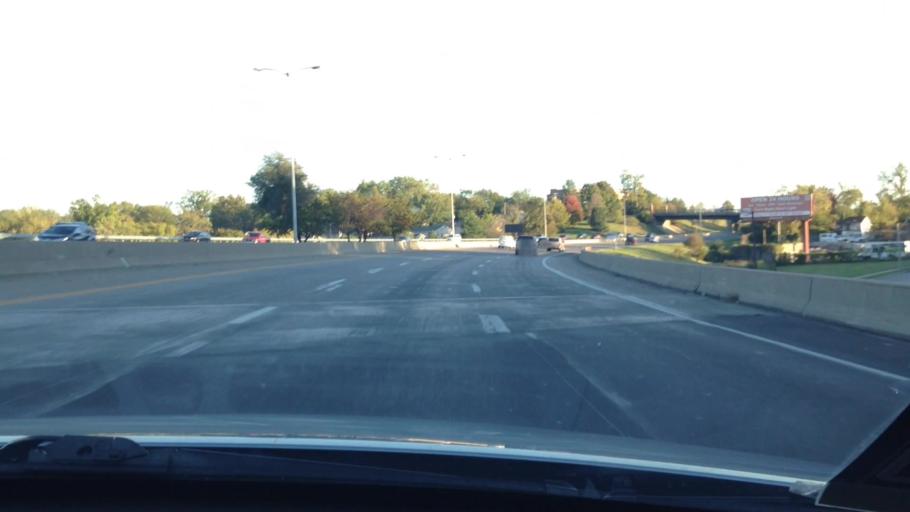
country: US
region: Kansas
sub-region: Johnson County
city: Westwood
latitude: 39.0370
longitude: -94.5551
